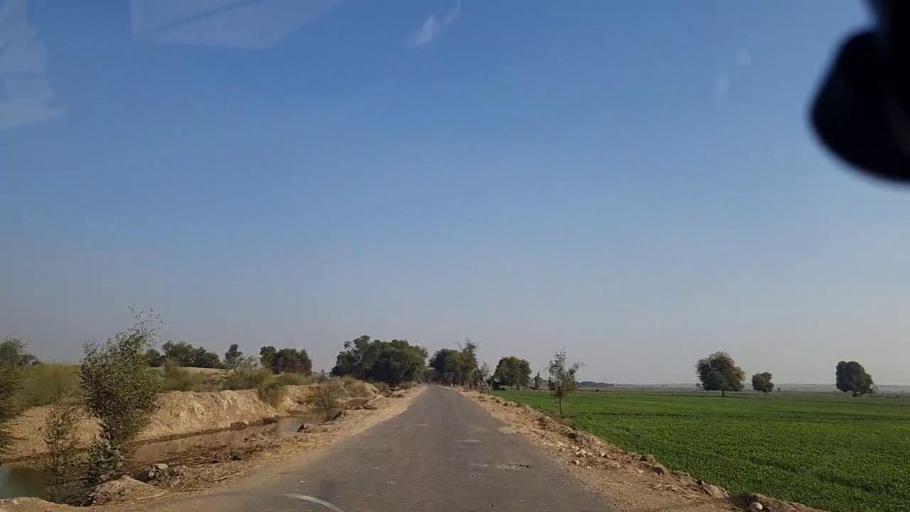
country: PK
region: Sindh
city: Khanpur
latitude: 27.6805
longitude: 69.5567
